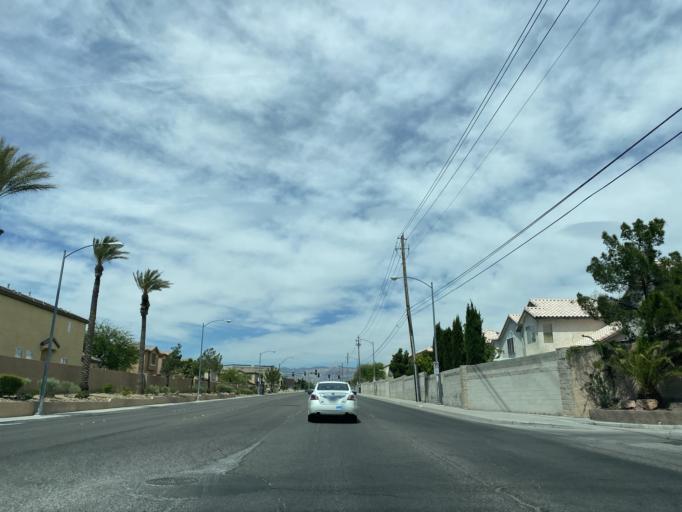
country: US
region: Nevada
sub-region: Clark County
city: Spring Valley
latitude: 36.1257
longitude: -115.2677
